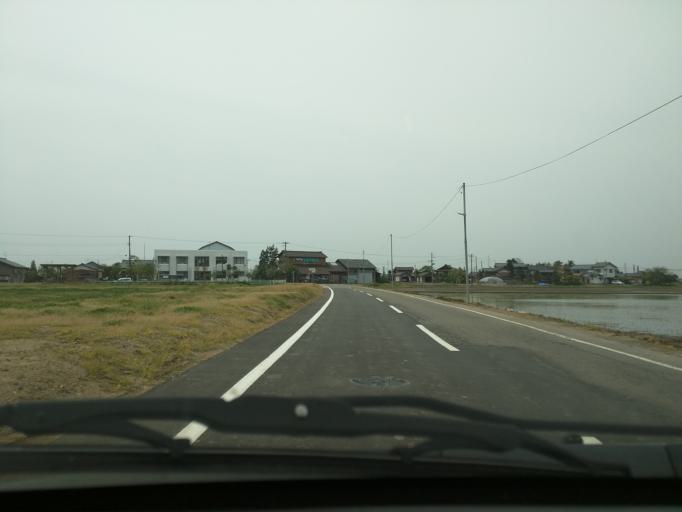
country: JP
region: Niigata
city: Mitsuke
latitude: 37.5527
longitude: 138.9178
